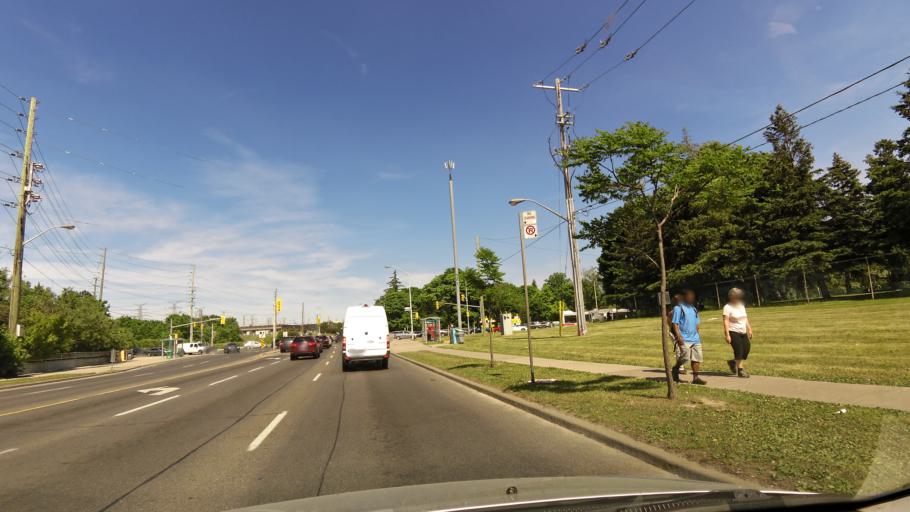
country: CA
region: Ontario
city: Concord
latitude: 43.7752
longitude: -79.5228
